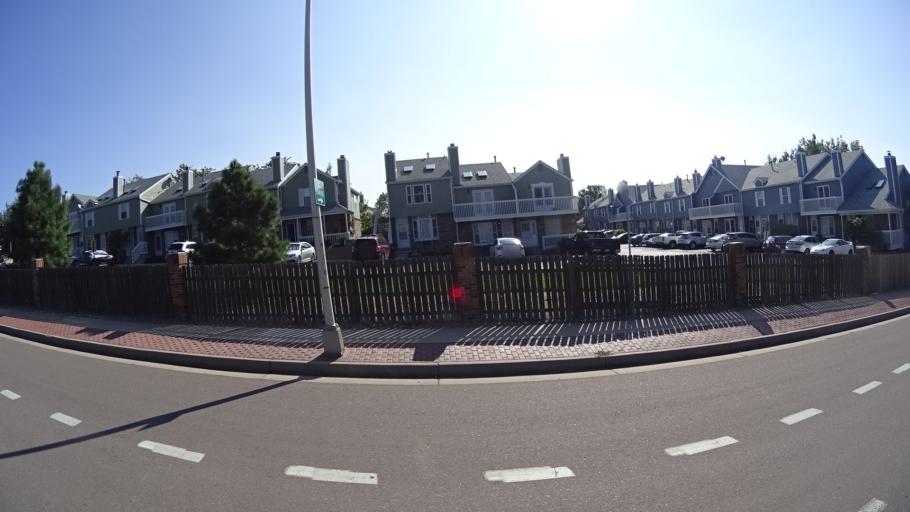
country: US
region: Colorado
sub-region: El Paso County
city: Colorado Springs
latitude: 38.8274
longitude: -104.8592
